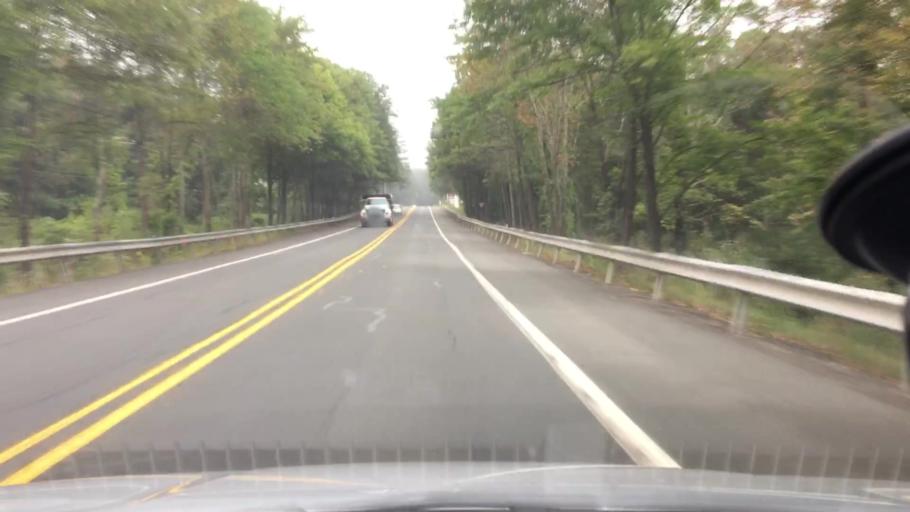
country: US
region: Pennsylvania
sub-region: Monroe County
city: Mountainhome
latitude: 41.1418
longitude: -75.2887
